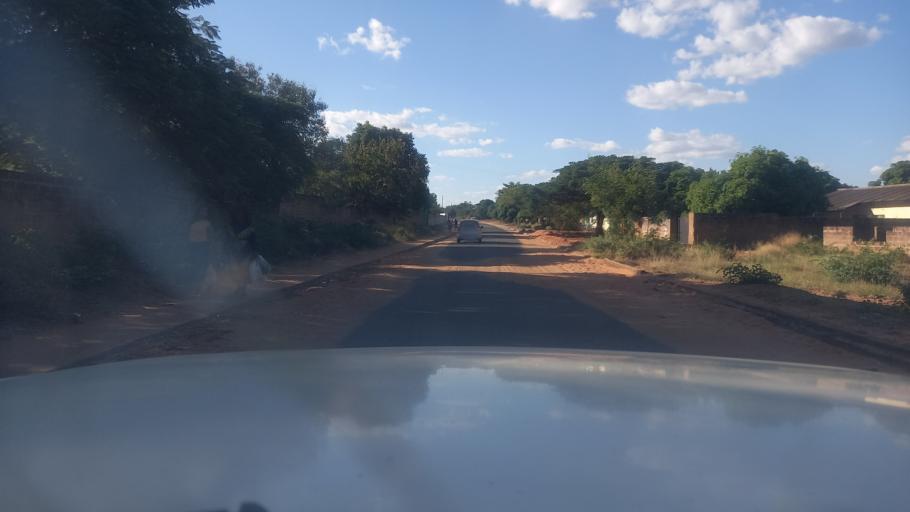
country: ZM
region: Southern
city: Livingstone
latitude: -17.8327
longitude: 25.8658
